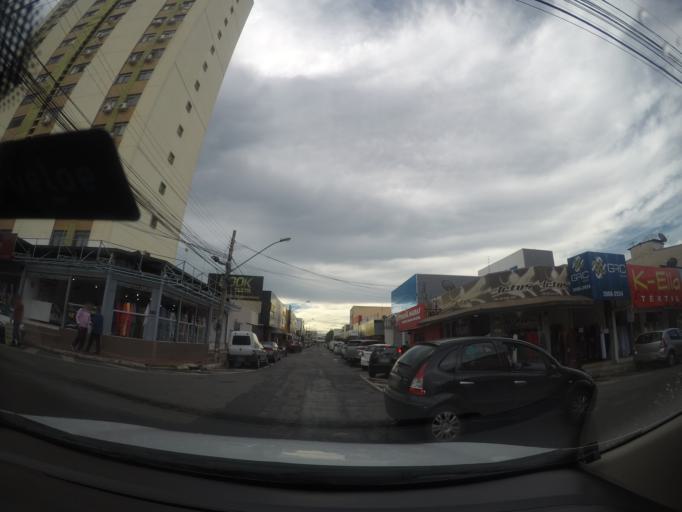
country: BR
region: Goias
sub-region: Goiania
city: Goiania
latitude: -16.6706
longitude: -49.2915
